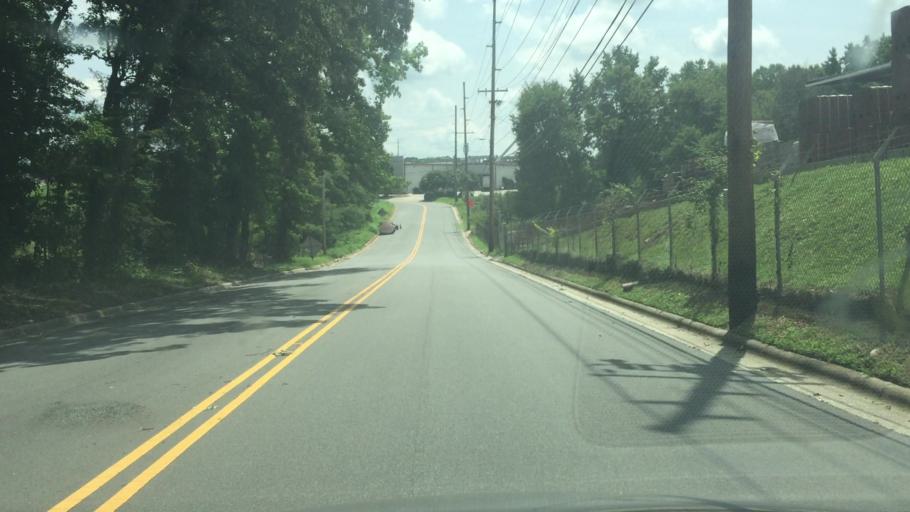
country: US
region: North Carolina
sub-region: Cabarrus County
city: Concord
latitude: 35.4352
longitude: -80.6063
